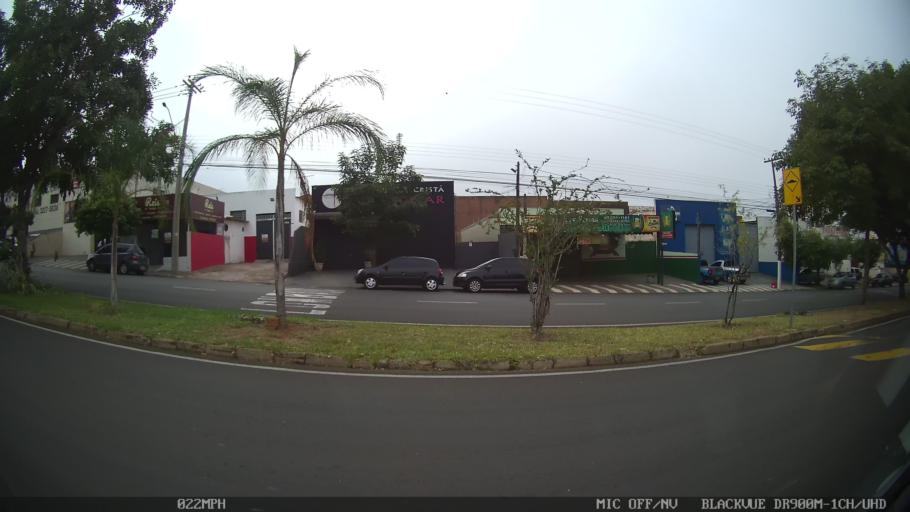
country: BR
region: Sao Paulo
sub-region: Sao Jose Do Rio Preto
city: Sao Jose do Rio Preto
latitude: -20.8450
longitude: -49.3703
